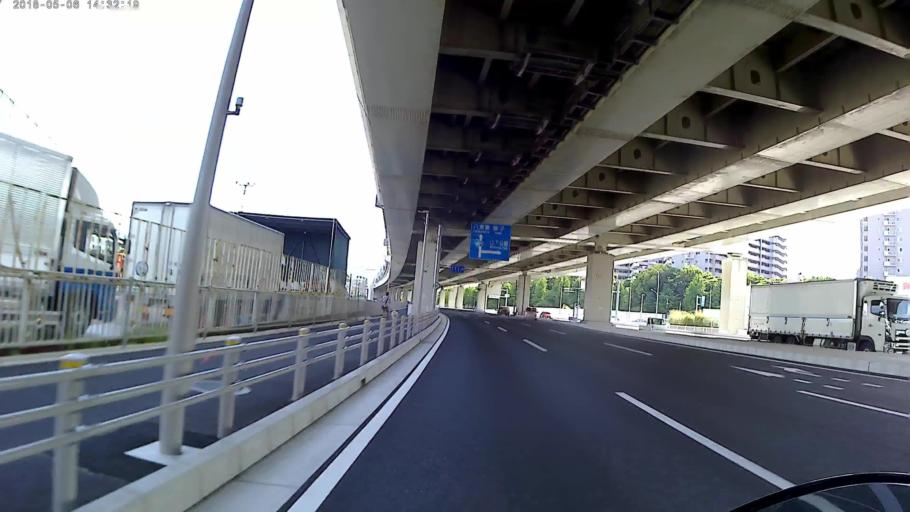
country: JP
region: Kanagawa
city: Yokohama
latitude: 35.4263
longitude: 139.6712
